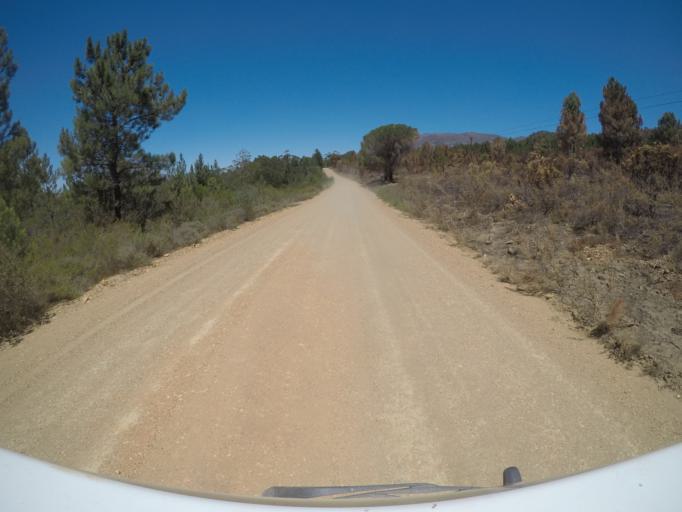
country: ZA
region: Western Cape
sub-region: Overberg District Municipality
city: Grabouw
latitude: -34.1599
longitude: 19.2260
